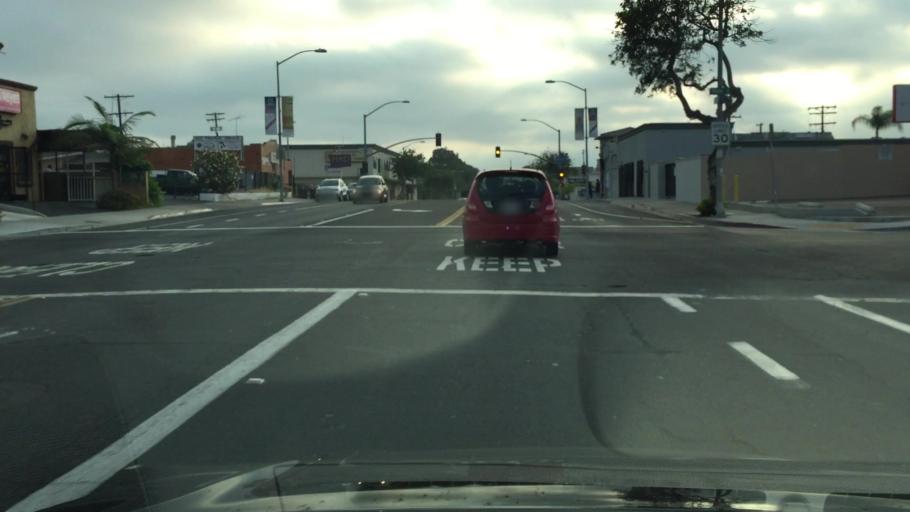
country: US
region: California
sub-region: San Diego County
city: National City
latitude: 32.7115
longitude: -117.1043
